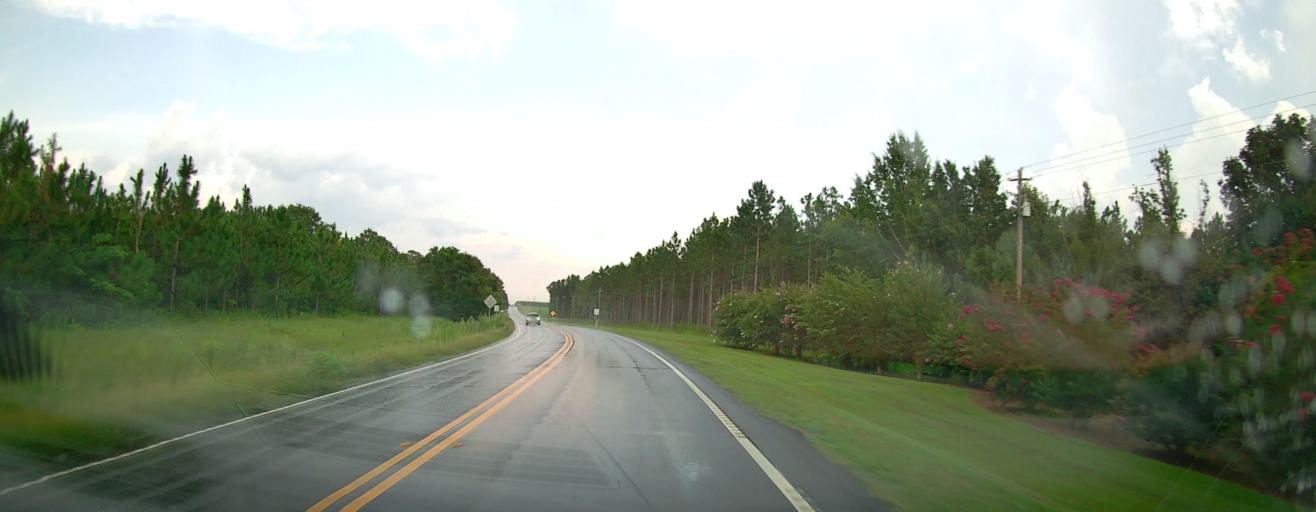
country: US
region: Georgia
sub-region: Dodge County
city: Chester
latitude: 32.5547
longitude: -83.1467
